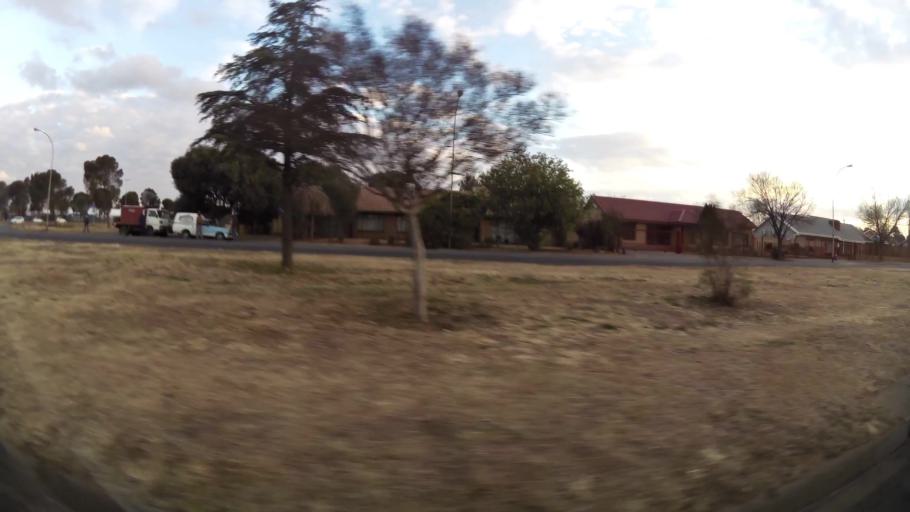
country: ZA
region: Orange Free State
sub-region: Mangaung Metropolitan Municipality
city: Bloemfontein
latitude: -29.1557
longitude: 26.1871
